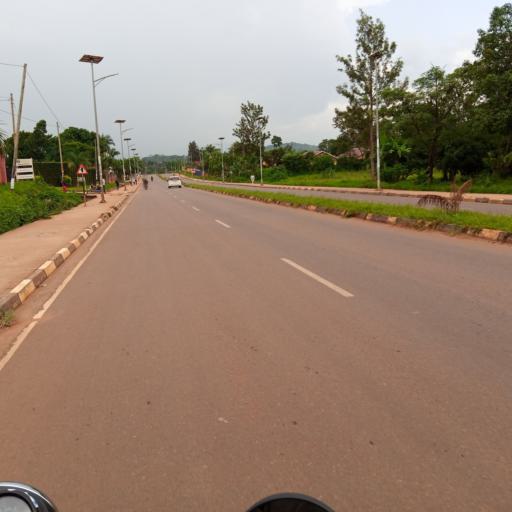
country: UG
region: Eastern Region
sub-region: Mbale District
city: Mbale
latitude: 1.0805
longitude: 34.1750
